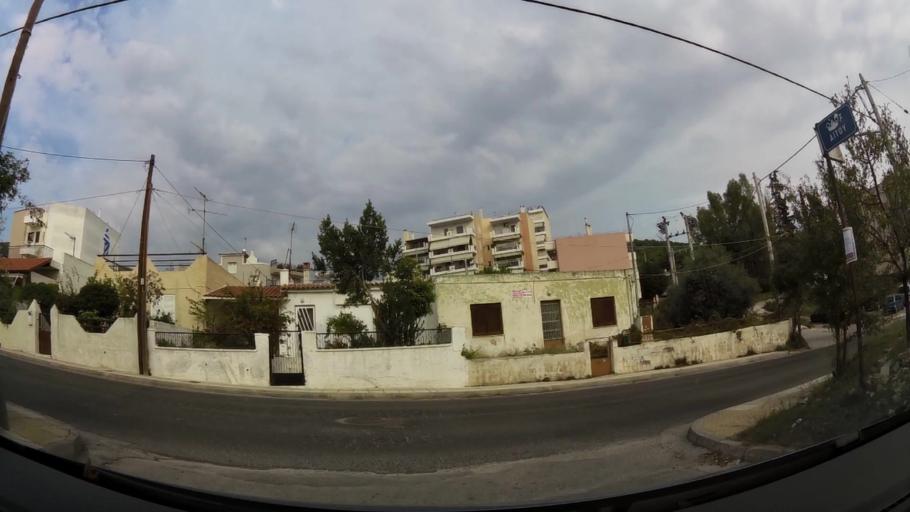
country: GR
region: Attica
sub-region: Nomarchia Athinas
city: Kamateron
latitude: 38.0604
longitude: 23.7046
